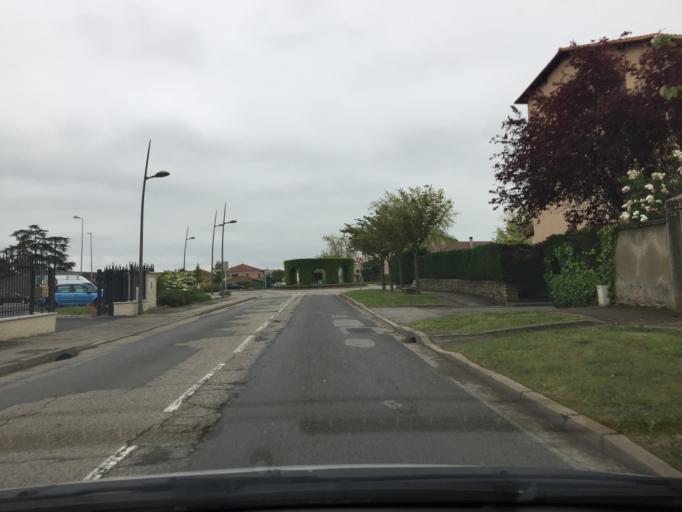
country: FR
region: Rhone-Alpes
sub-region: Departement du Rhone
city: Mornant
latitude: 45.6226
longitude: 4.6701
